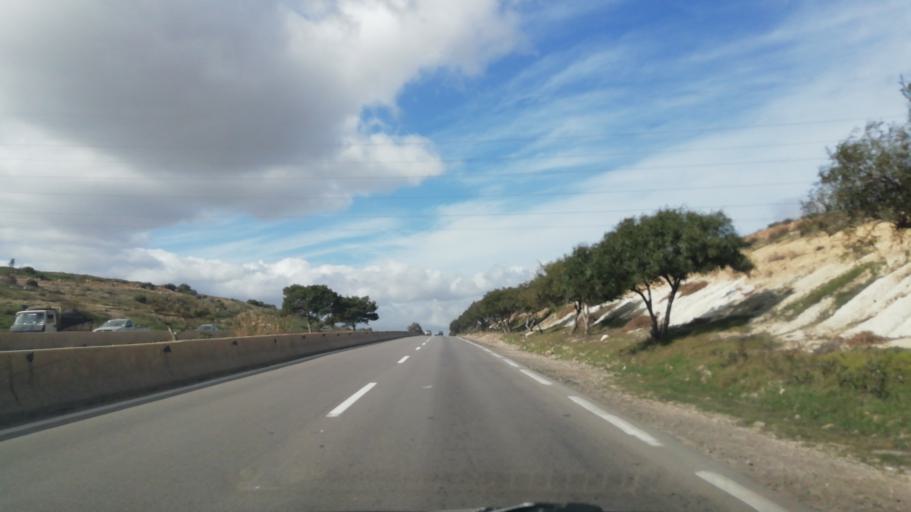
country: DZ
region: Oran
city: Ain el Bya
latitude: 35.7714
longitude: -0.2421
